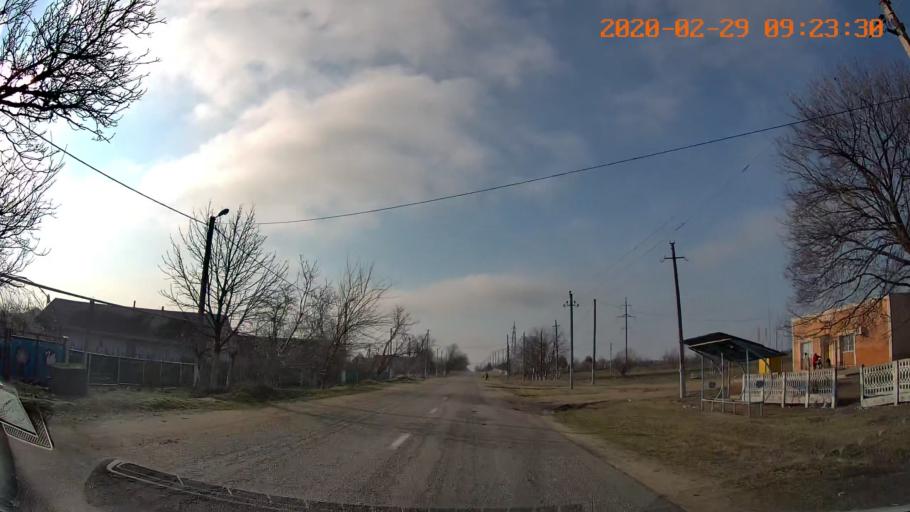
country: MD
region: Telenesti
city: Pervomaisc
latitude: 46.7252
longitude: 29.9611
